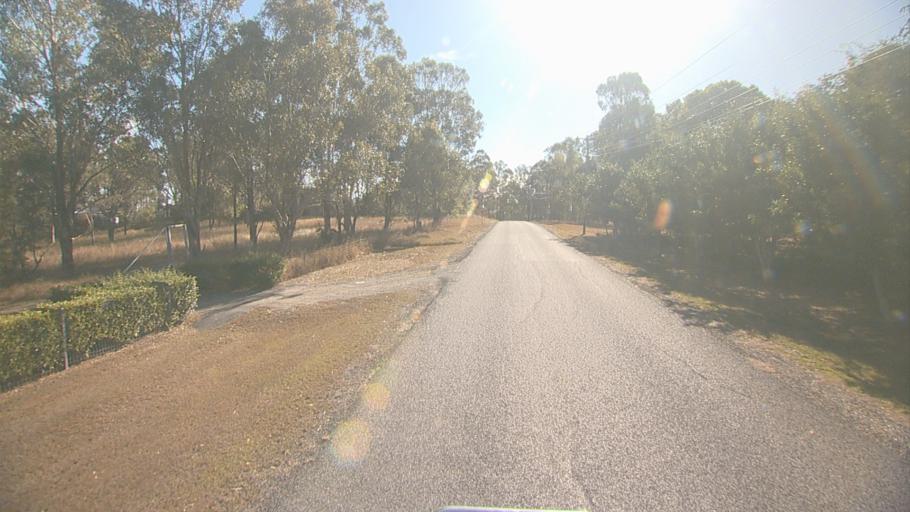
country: AU
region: Queensland
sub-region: Logan
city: Cedar Vale
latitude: -27.8637
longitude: 152.9849
